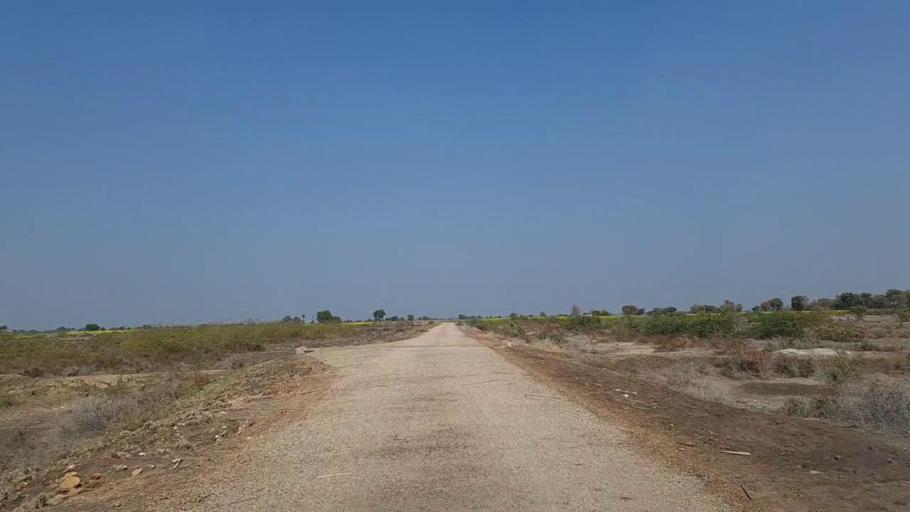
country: PK
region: Sindh
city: Nawabshah
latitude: 26.2921
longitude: 68.4810
